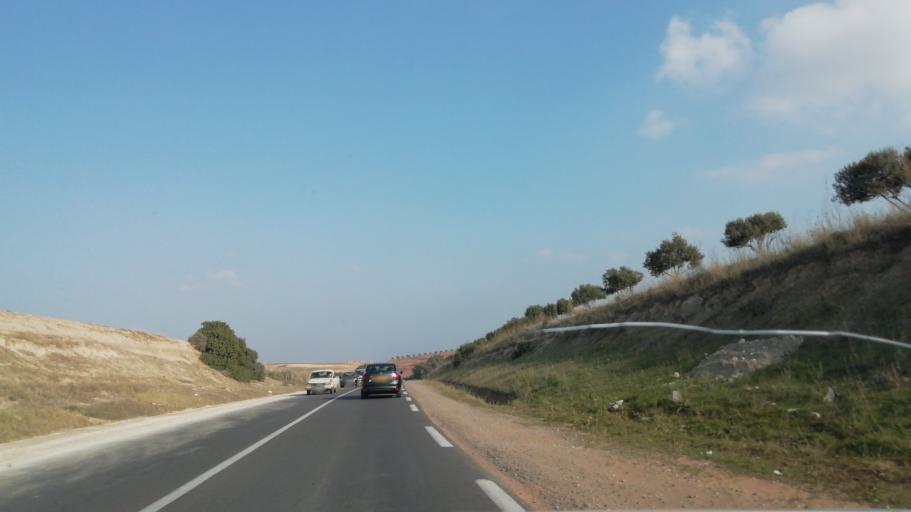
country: DZ
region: Ain Temouchent
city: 'Ain Temouchent
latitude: 35.3019
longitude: -1.0754
